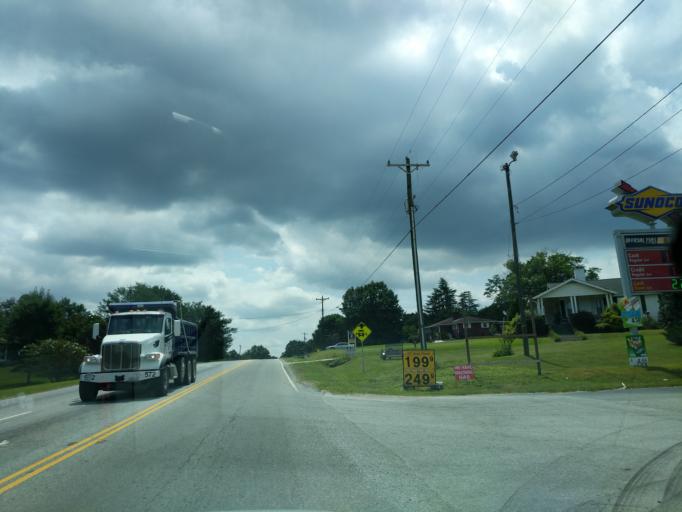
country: US
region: South Carolina
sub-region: Spartanburg County
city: Wellford
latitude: 34.9955
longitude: -82.1115
